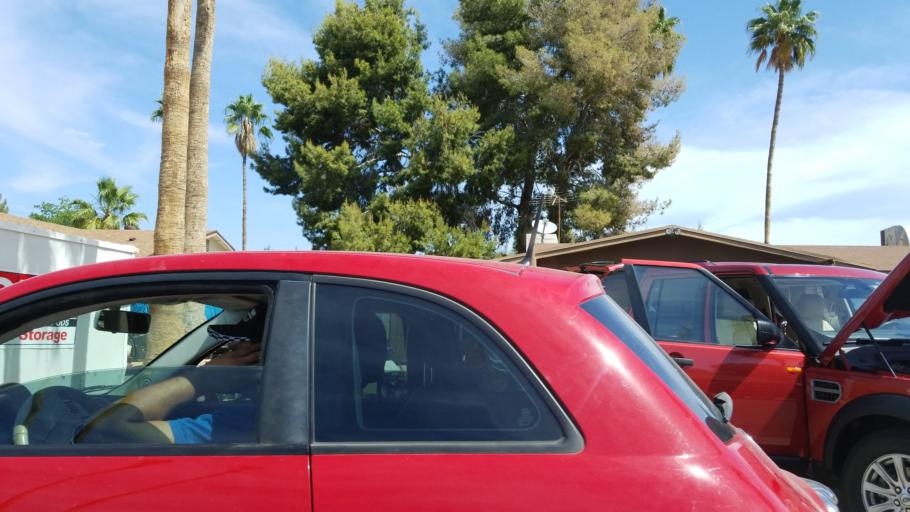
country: US
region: Arizona
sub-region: Maricopa County
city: Paradise Valley
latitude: 33.6123
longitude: -111.9687
